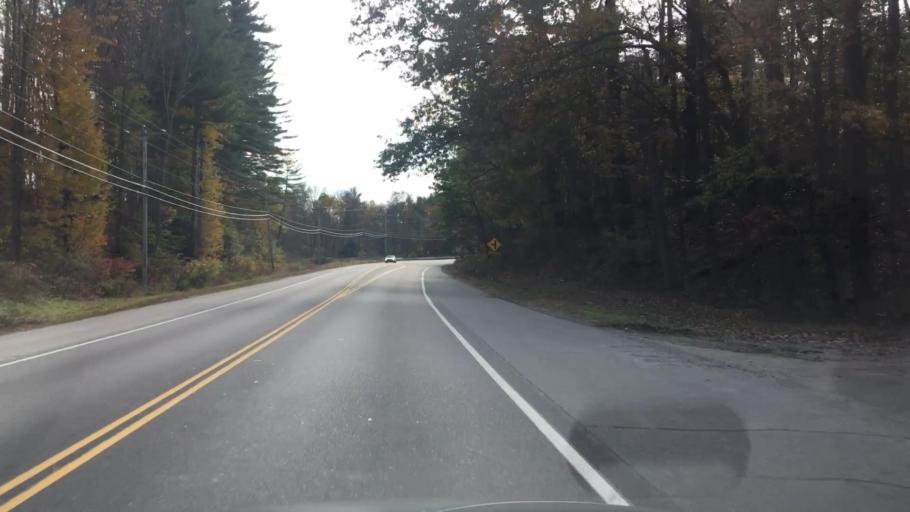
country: US
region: New Hampshire
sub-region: Hillsborough County
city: Milford
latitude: 42.8825
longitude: -71.6090
